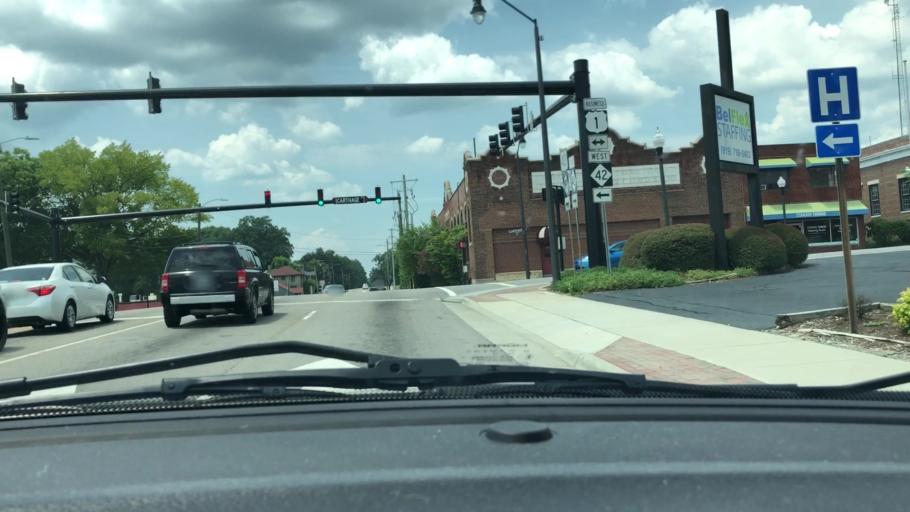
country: US
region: North Carolina
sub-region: Lee County
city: Sanford
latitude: 35.4797
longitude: -79.1802
